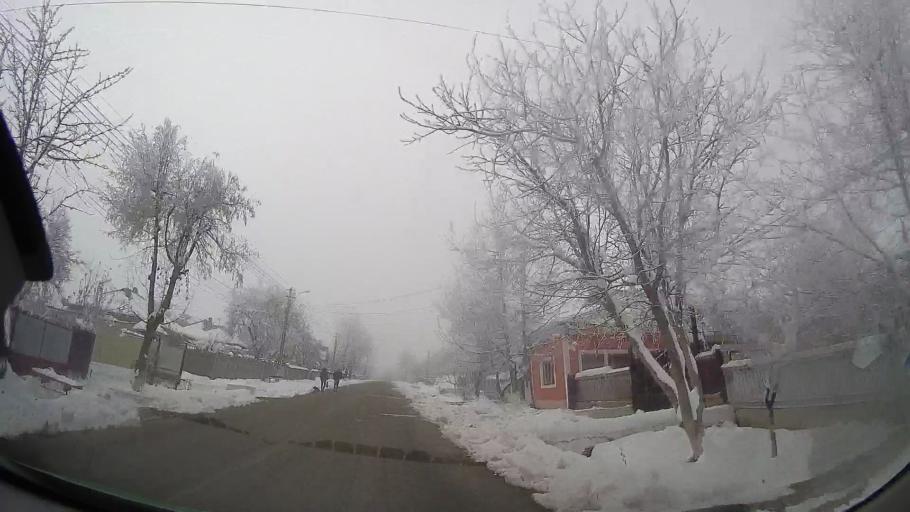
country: RO
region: Iasi
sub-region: Comuna Valea Seaca
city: Valea Seaca
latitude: 47.2940
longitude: 26.6715
